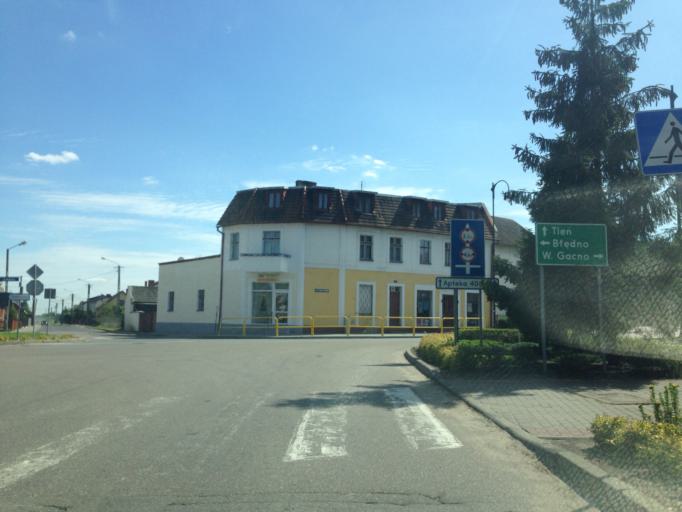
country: PL
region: Kujawsko-Pomorskie
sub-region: Powiat tucholski
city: Sliwice
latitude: 53.7086
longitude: 18.1733
